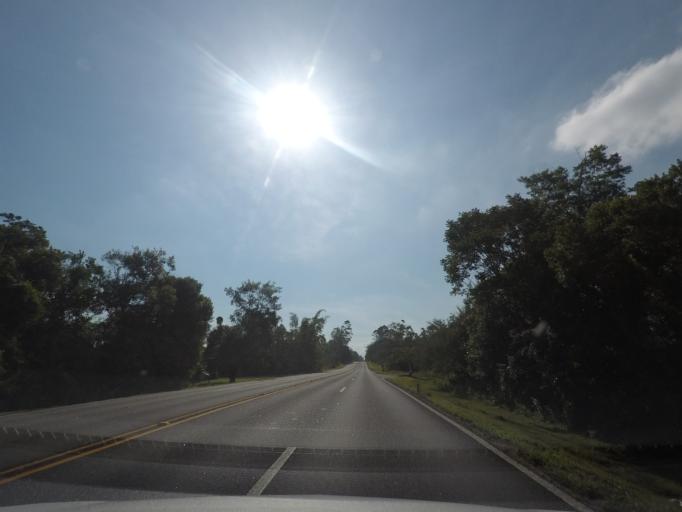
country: BR
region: Parana
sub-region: Pontal Do Parana
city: Pontal do Parana
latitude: -25.6114
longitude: -48.6045
